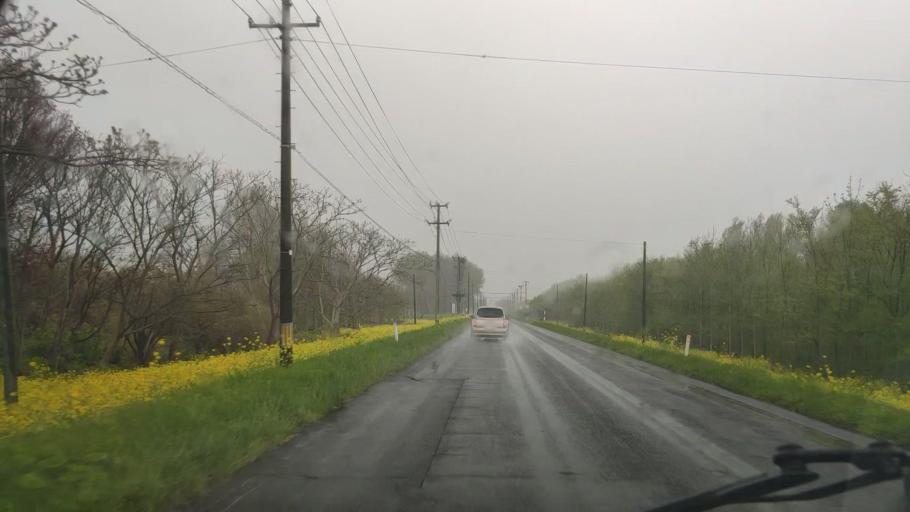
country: JP
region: Akita
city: Tenno
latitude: 39.9510
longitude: 139.9459
